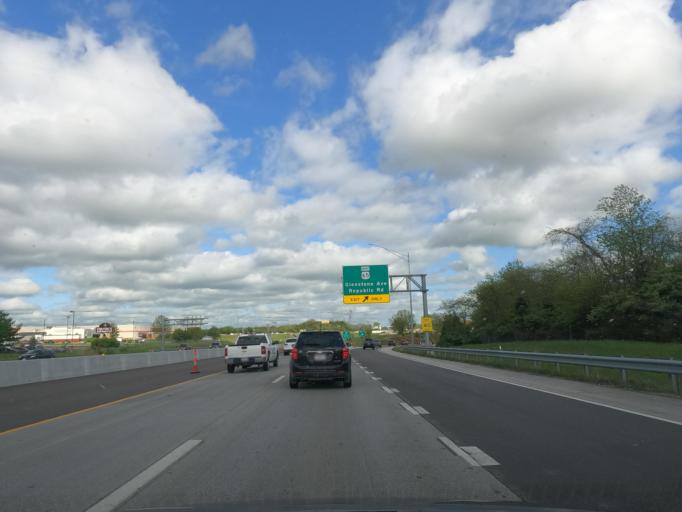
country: US
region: Missouri
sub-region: Greene County
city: Springfield
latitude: 37.1403
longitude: -93.2597
